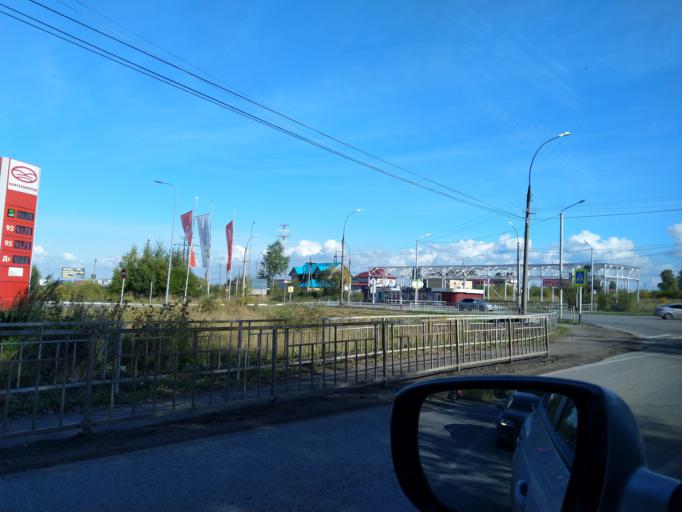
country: RU
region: Perm
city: Usol'ye
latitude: 59.4327
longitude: 56.6752
